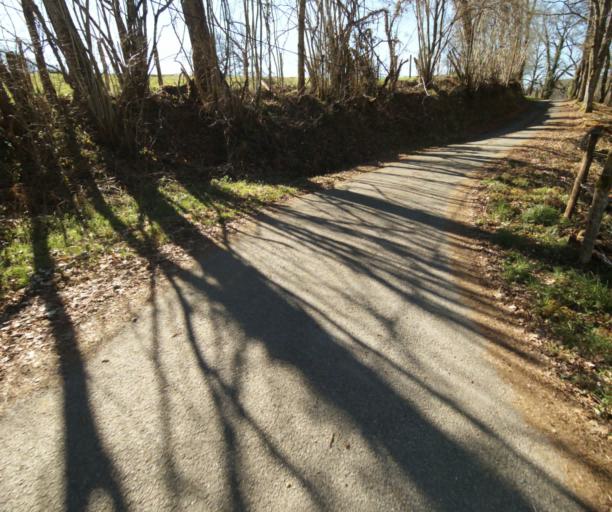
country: FR
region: Limousin
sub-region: Departement de la Correze
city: Chamboulive
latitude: 45.4037
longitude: 1.6984
